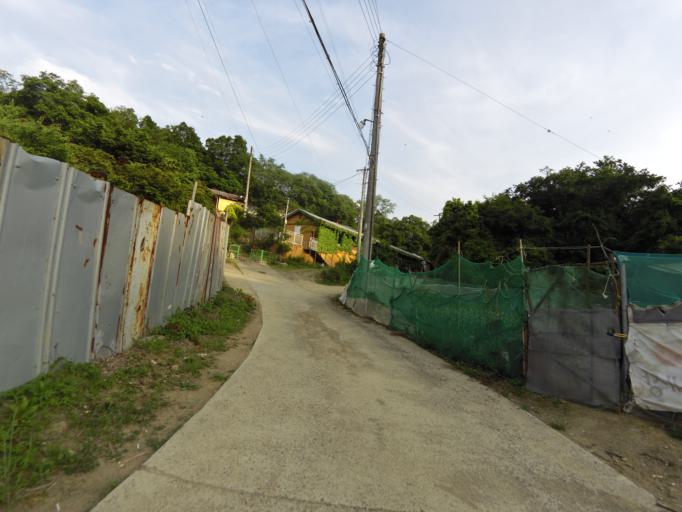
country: KR
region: Daegu
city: Daegu
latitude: 35.8599
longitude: 128.6503
